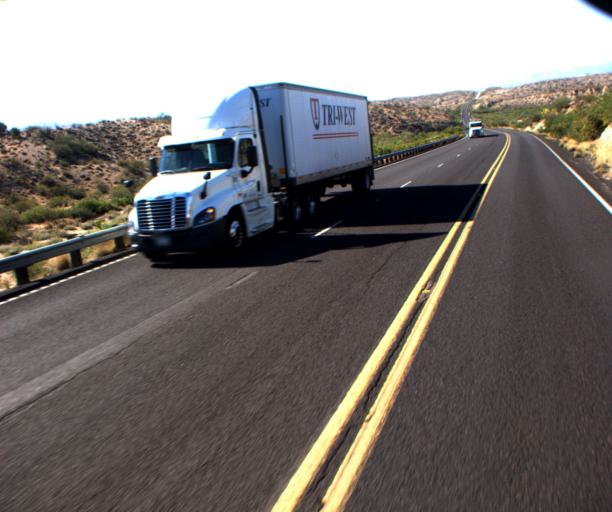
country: US
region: Arizona
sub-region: Mohave County
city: Kingman
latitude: 34.9264
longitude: -113.6587
